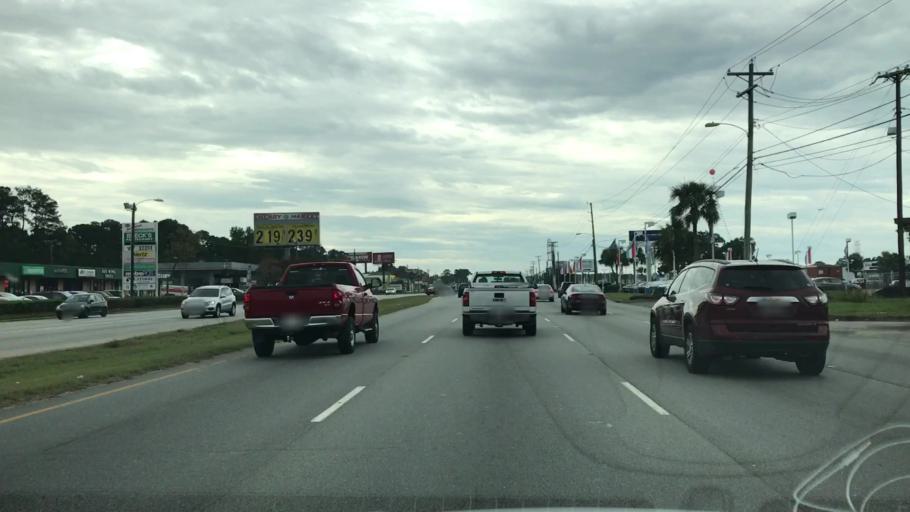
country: US
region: South Carolina
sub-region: Berkeley County
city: Goose Creek
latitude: 32.9620
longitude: -80.0438
